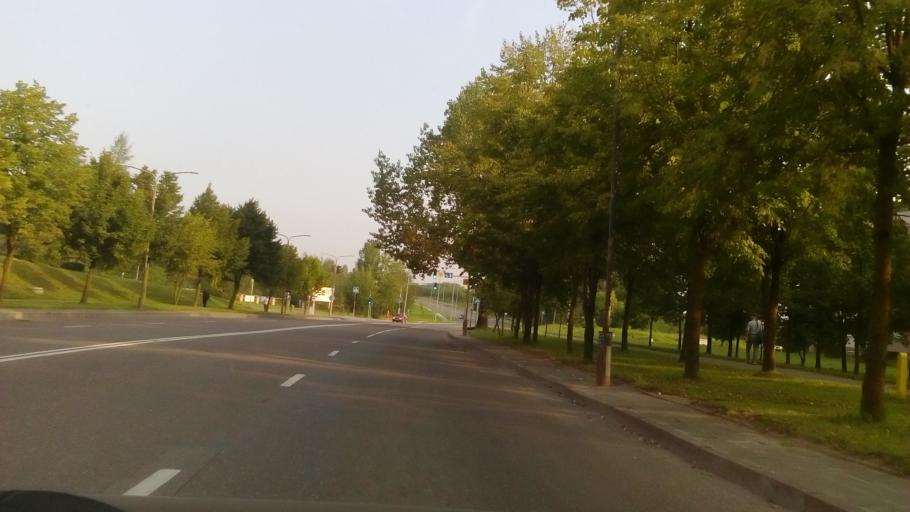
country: LT
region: Alytaus apskritis
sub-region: Alytus
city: Alytus
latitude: 54.3983
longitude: 24.0154
